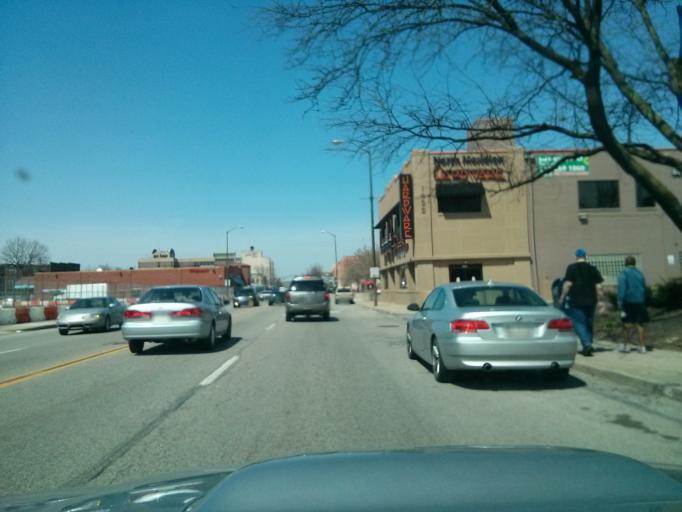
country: US
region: Indiana
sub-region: Marion County
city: Indianapolis
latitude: 39.7864
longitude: -86.1573
